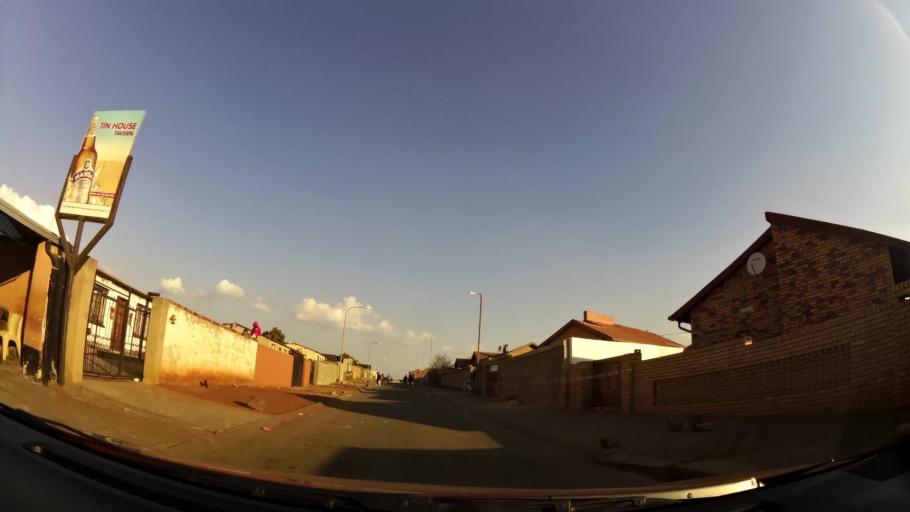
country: ZA
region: Gauteng
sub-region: City of Johannesburg Metropolitan Municipality
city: Soweto
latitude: -26.2264
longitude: 27.8576
